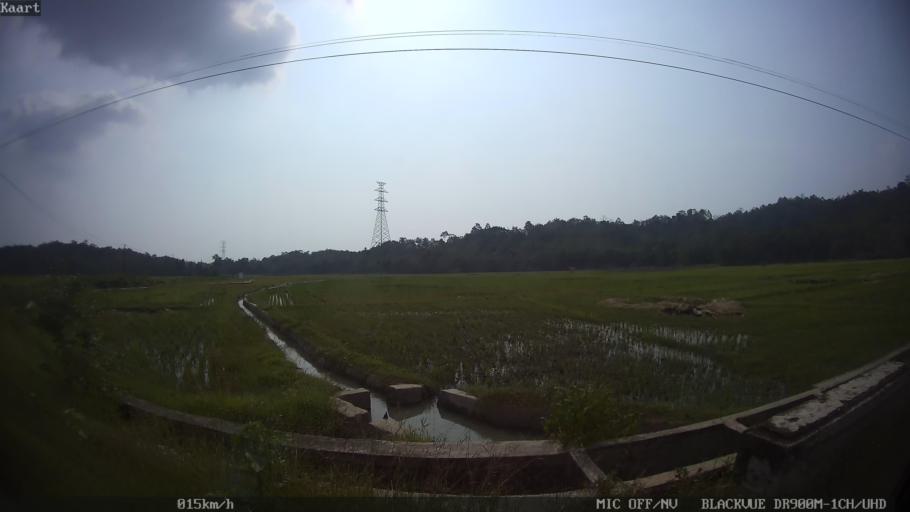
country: ID
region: Lampung
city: Gadingrejo
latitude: -5.4060
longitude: 105.0195
